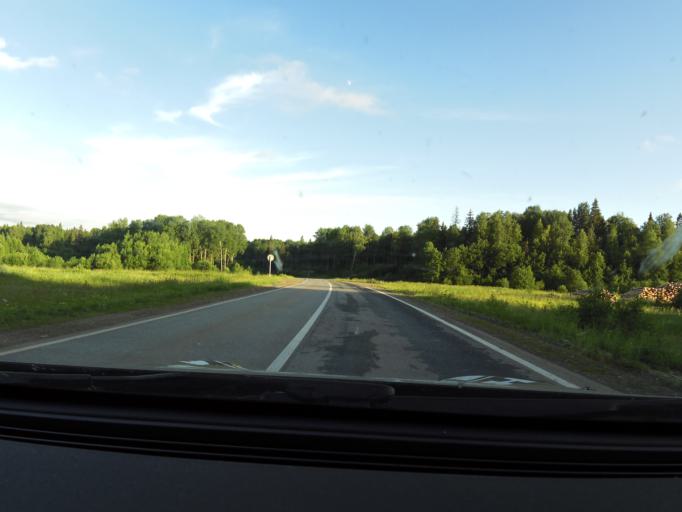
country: RU
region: Kirov
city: Kostino
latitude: 58.6847
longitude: 53.7380
